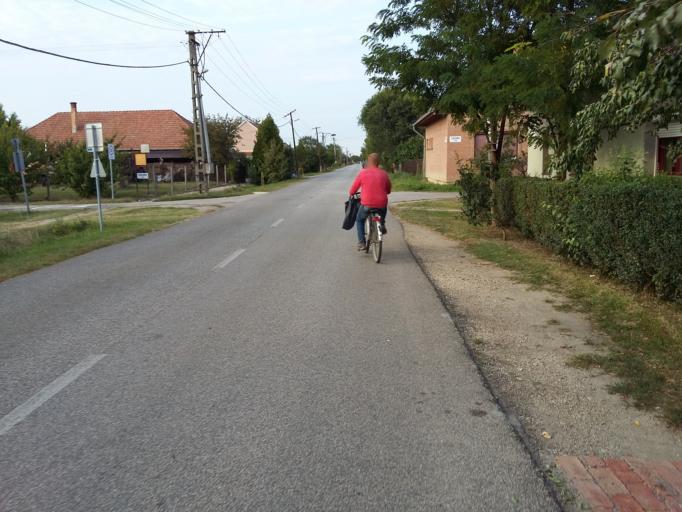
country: HU
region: Csongrad
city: Szeged
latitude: 46.2066
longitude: 20.1066
